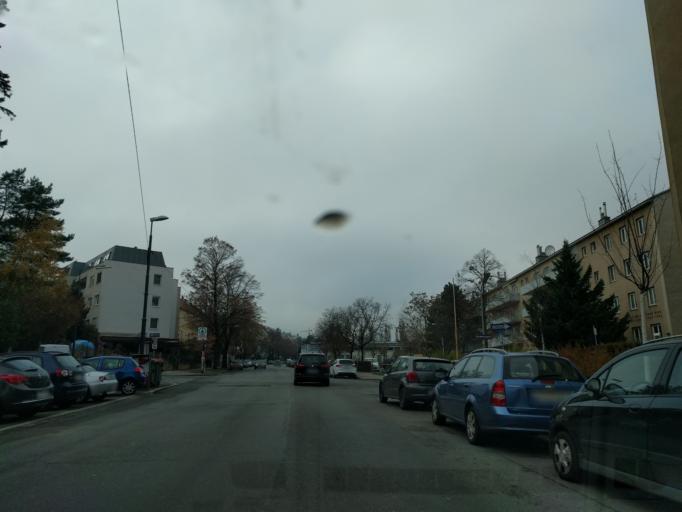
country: AT
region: Vienna
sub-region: Wien Stadt
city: Vienna
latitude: 48.2418
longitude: 16.3285
